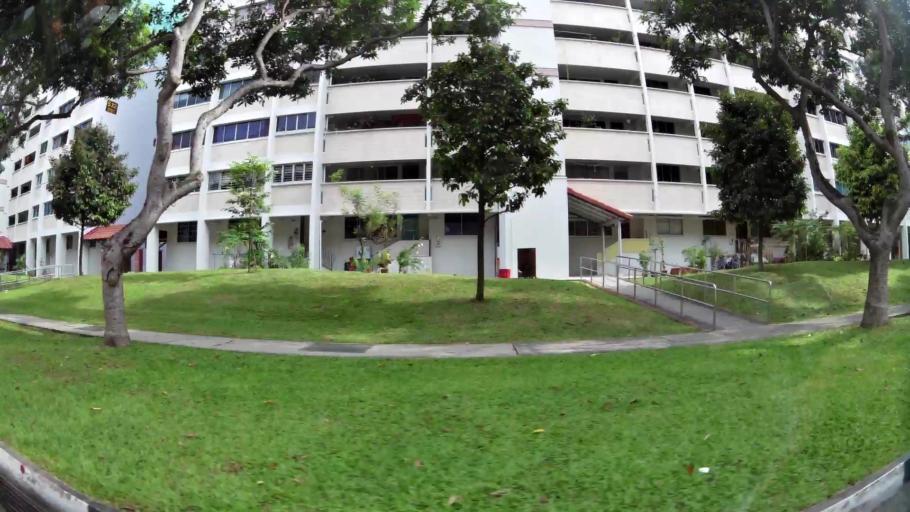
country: SG
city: Singapore
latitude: 1.3760
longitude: 103.8903
